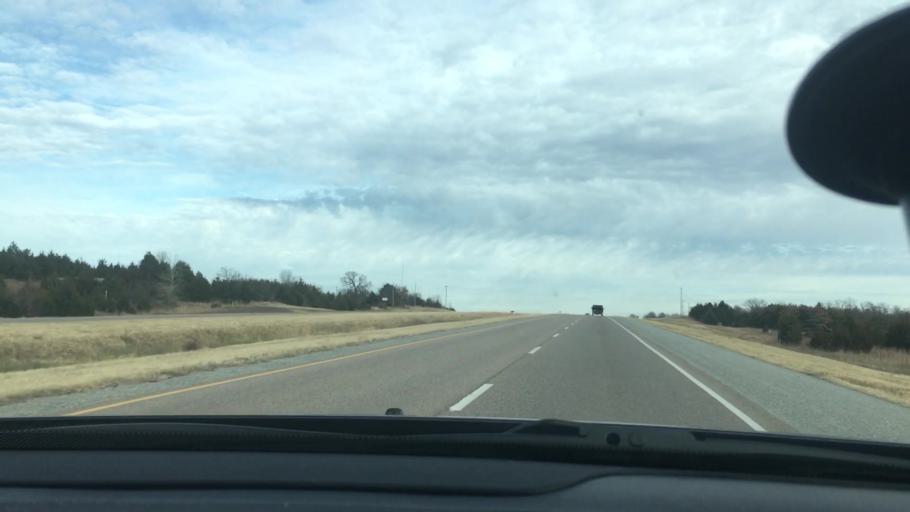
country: US
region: Oklahoma
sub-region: Pontotoc County
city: Byng
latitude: 34.8703
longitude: -96.6788
